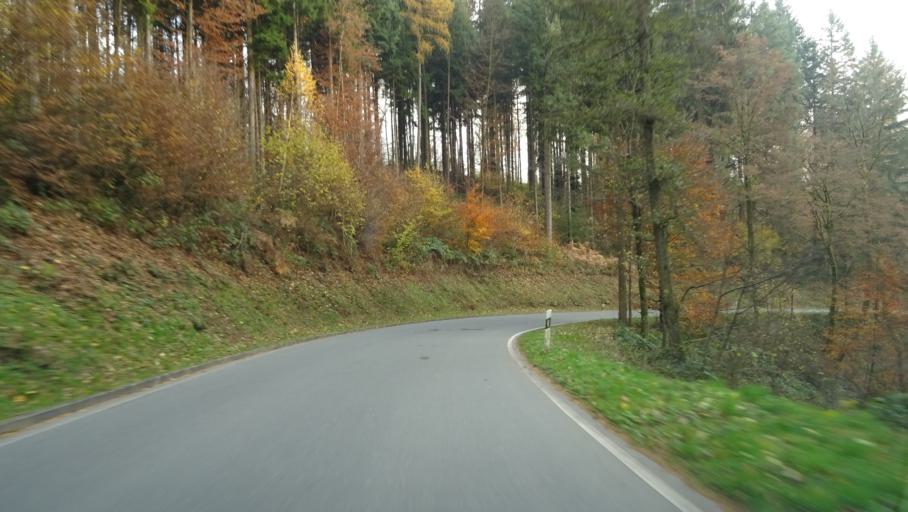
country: DE
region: Baden-Wuerttemberg
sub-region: Karlsruhe Region
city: Neckargerach
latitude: 49.4133
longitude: 9.0778
